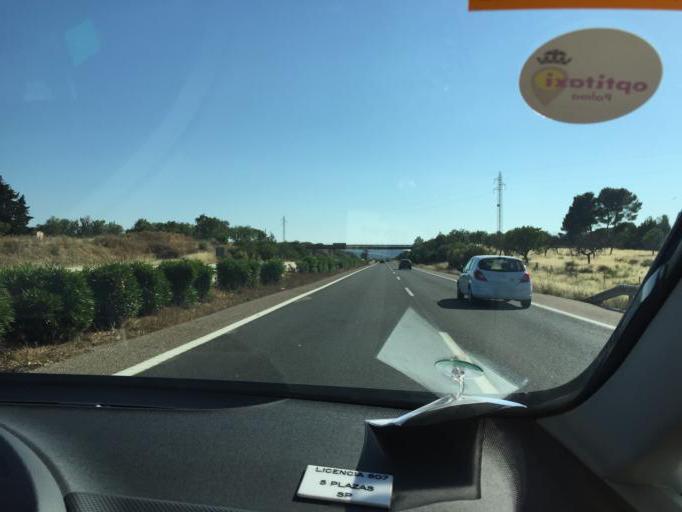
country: ES
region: Balearic Islands
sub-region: Illes Balears
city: Consell
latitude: 39.6662
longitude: 2.8188
